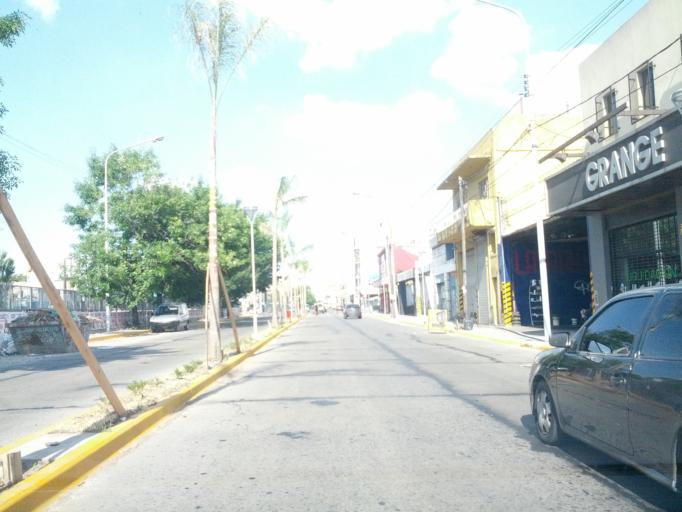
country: AR
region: Buenos Aires
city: San Justo
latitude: -34.6430
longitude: -58.5790
